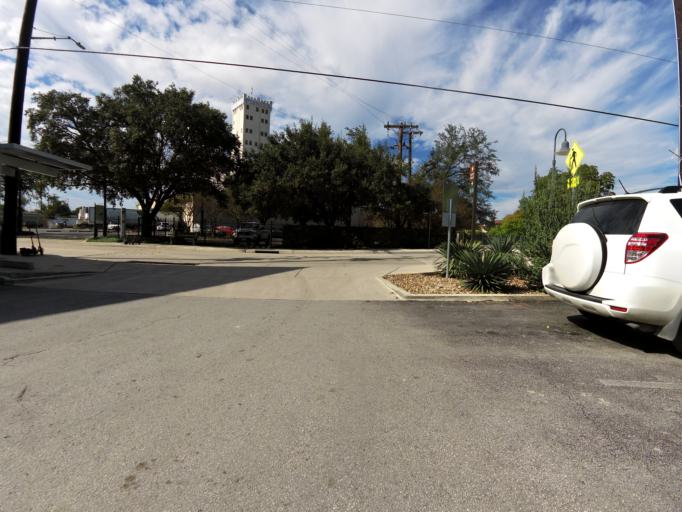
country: US
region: Texas
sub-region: Bexar County
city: San Antonio
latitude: 29.4100
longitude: -98.4953
